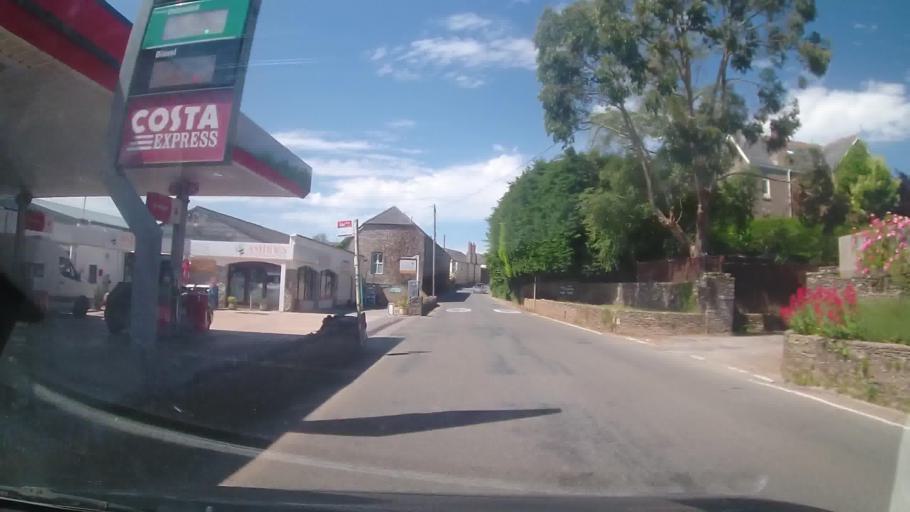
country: GB
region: England
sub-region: Devon
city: Kingsbridge
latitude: 50.2709
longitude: -3.7373
